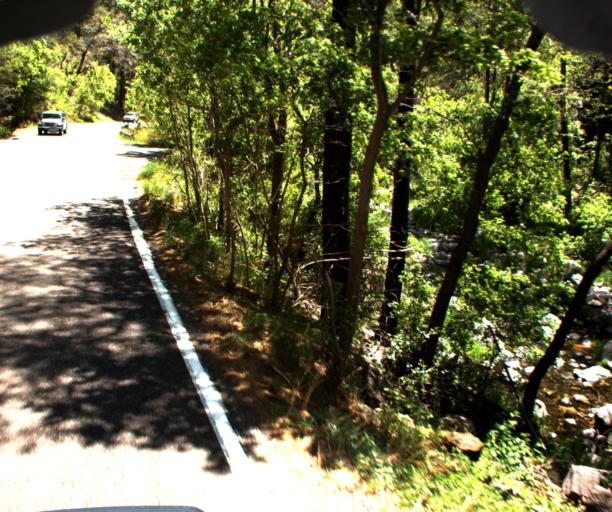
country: US
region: Arizona
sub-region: Coconino County
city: Kachina Village
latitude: 35.0058
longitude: -111.7347
